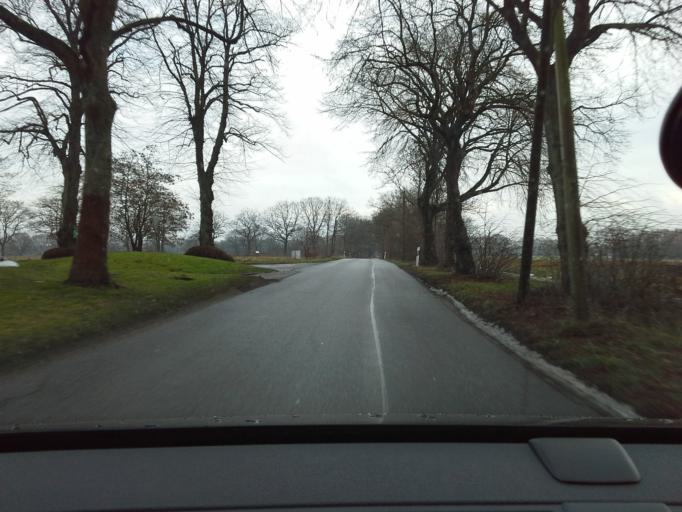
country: DE
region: Schleswig-Holstein
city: Henstedt-Ulzburg
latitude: 53.7462
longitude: 10.0178
